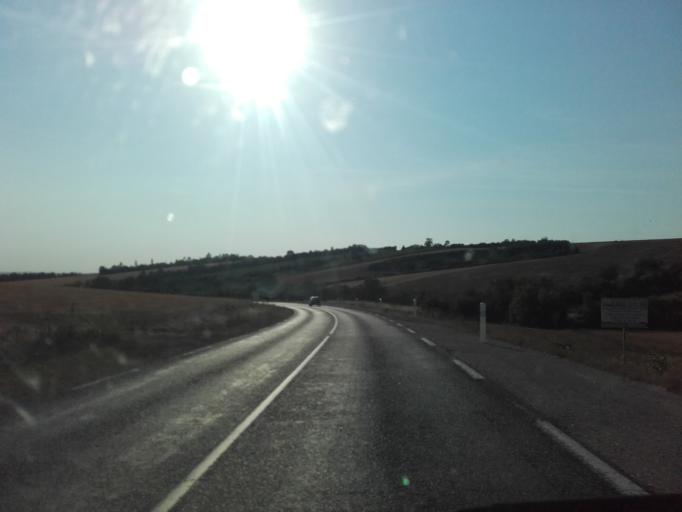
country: FR
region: Bourgogne
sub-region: Departement de l'Yonne
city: Venoy
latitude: 47.7953
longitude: 3.6422
